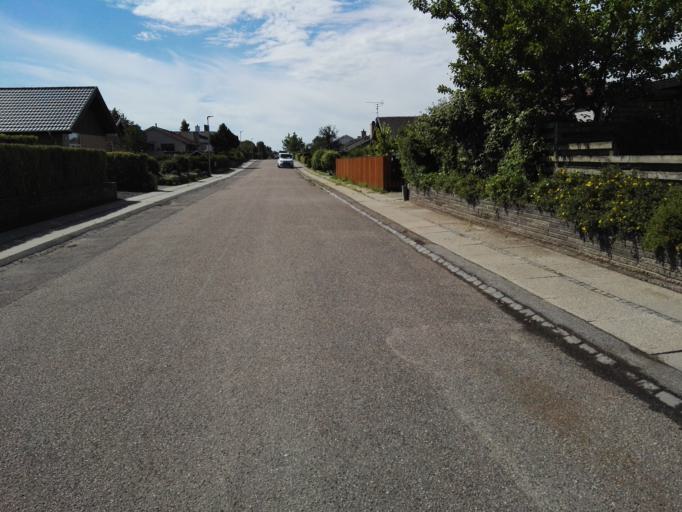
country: DK
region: Capital Region
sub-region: Egedal Kommune
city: Olstykke
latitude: 55.7970
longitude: 12.1443
